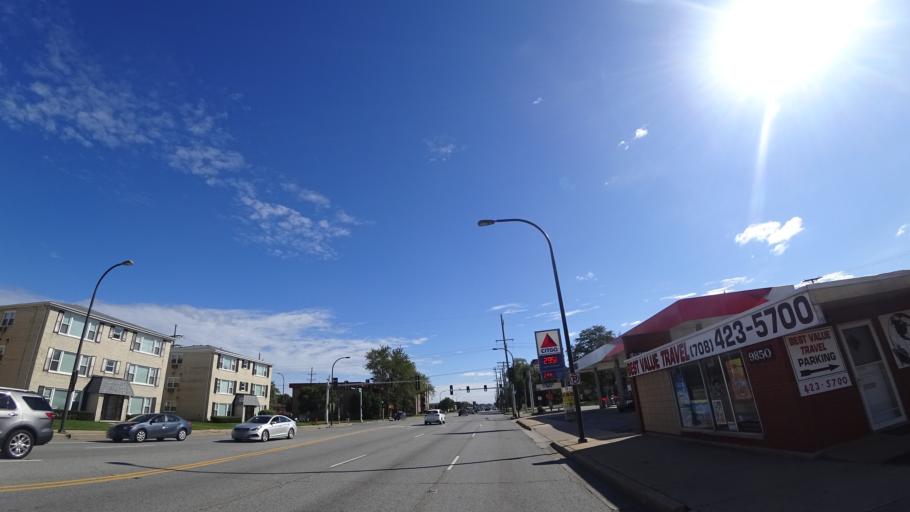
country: US
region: Illinois
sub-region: Cook County
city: Oak Lawn
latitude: 41.7135
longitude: -87.7407
